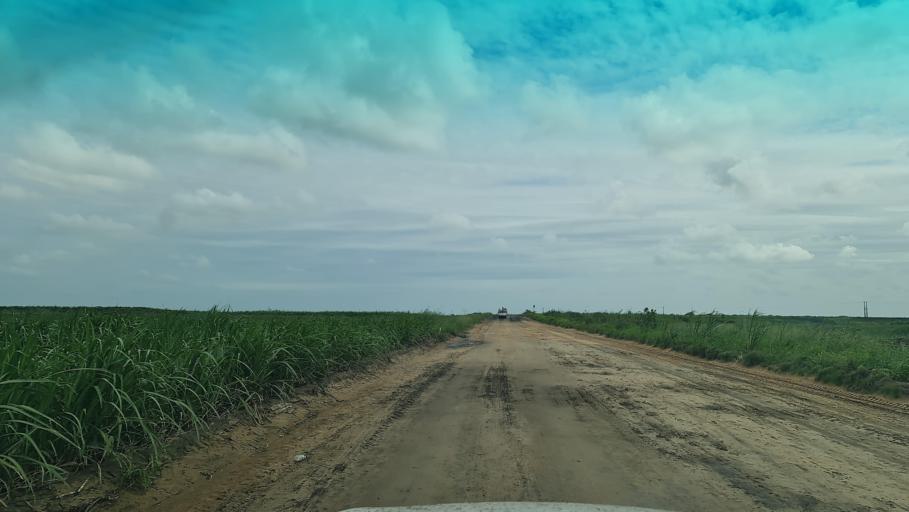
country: MZ
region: Maputo
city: Manhica
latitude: -25.4550
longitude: 32.8191
